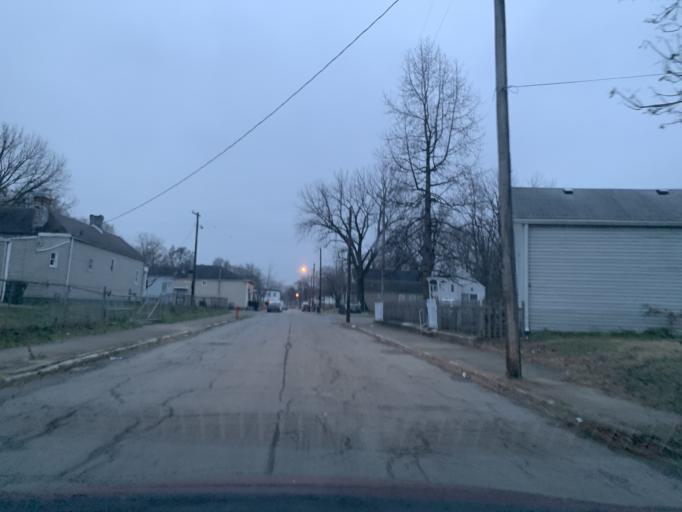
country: US
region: Kentucky
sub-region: Jefferson County
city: Louisville
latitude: 38.2642
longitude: -85.7835
